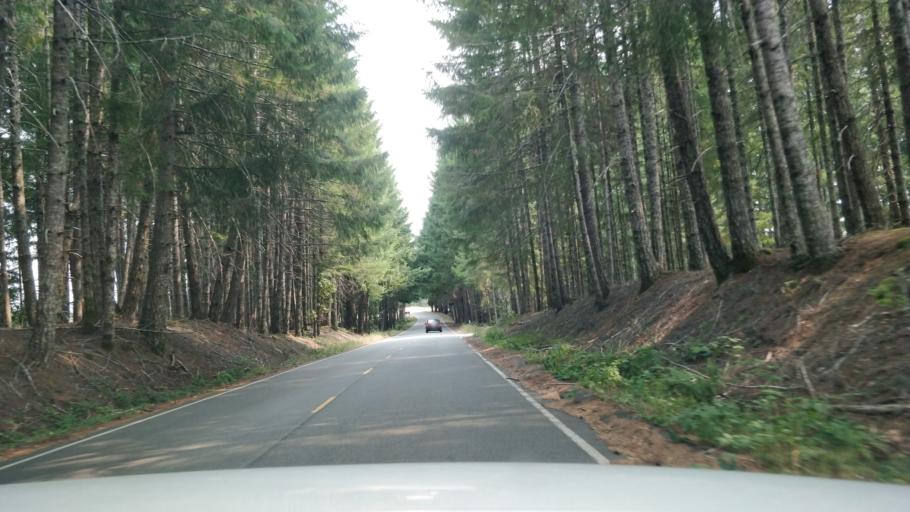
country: US
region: California
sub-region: Humboldt County
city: Westhaven-Moonstone
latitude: 41.2060
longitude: -123.9510
